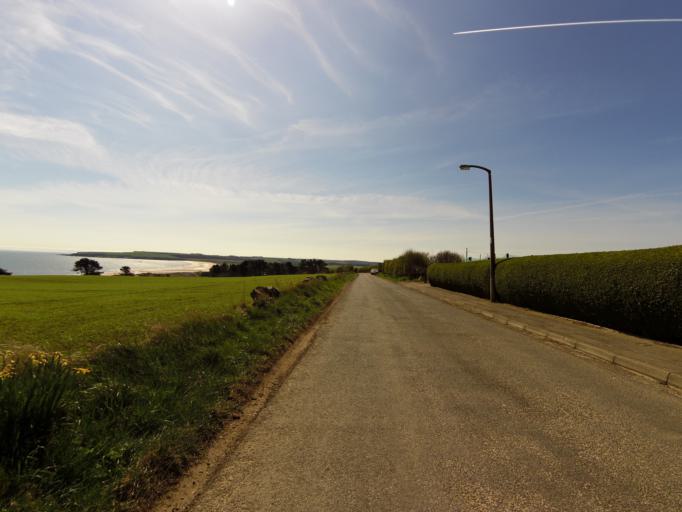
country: GB
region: Scotland
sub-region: Angus
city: Montrose
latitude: 56.6642
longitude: -2.5076
